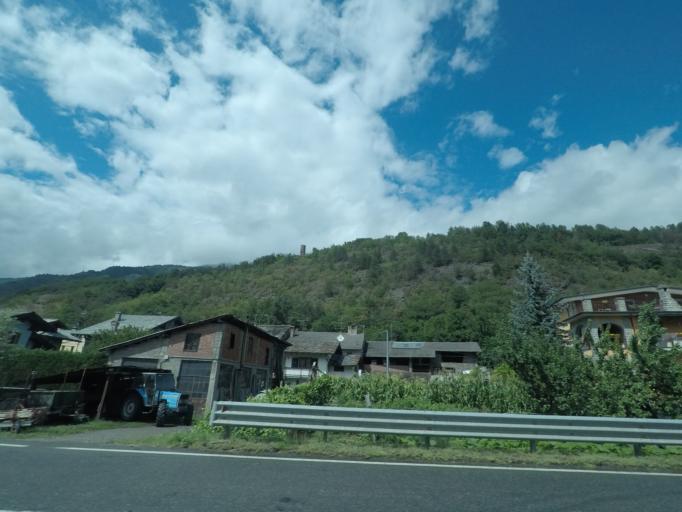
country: IT
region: Aosta Valley
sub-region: Valle d'Aosta
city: Villefranche
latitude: 45.7398
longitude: 7.4183
